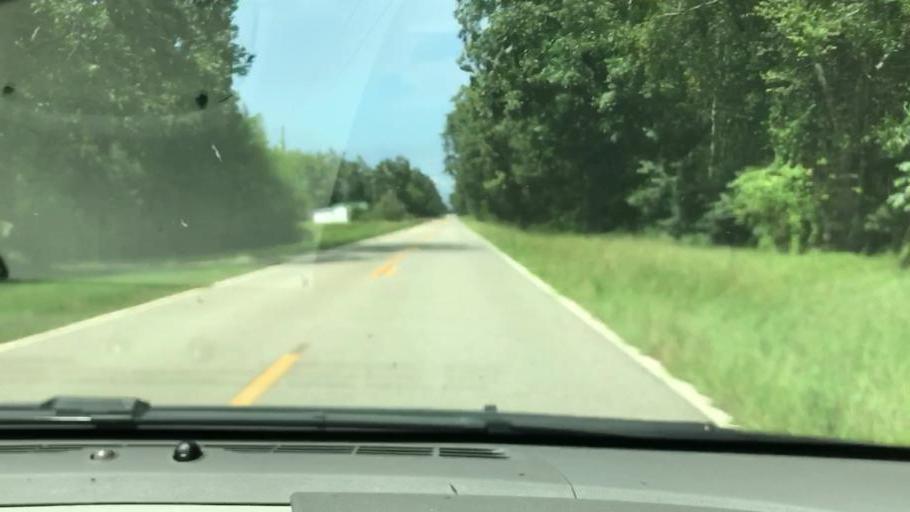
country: US
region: Georgia
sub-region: Seminole County
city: Donalsonville
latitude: 31.1337
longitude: -84.9953
